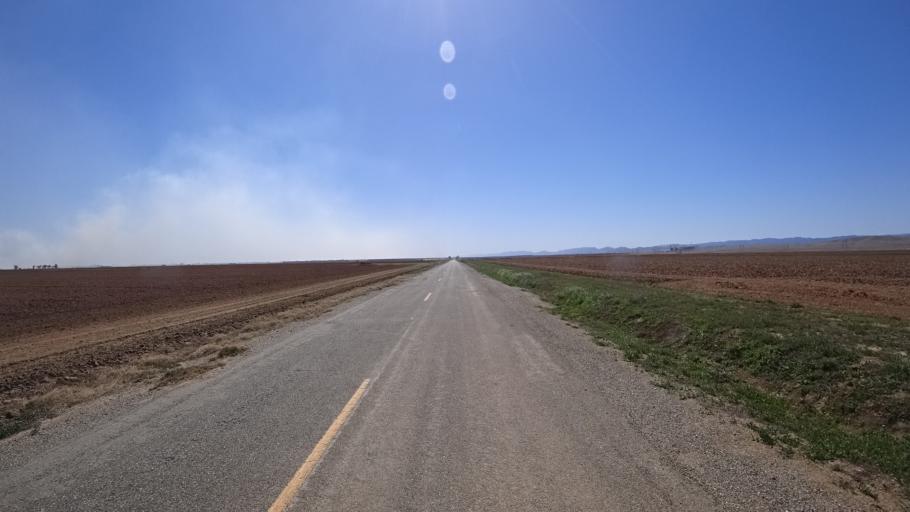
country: US
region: California
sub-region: Colusa County
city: Maxwell
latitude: 39.3918
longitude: -122.2483
